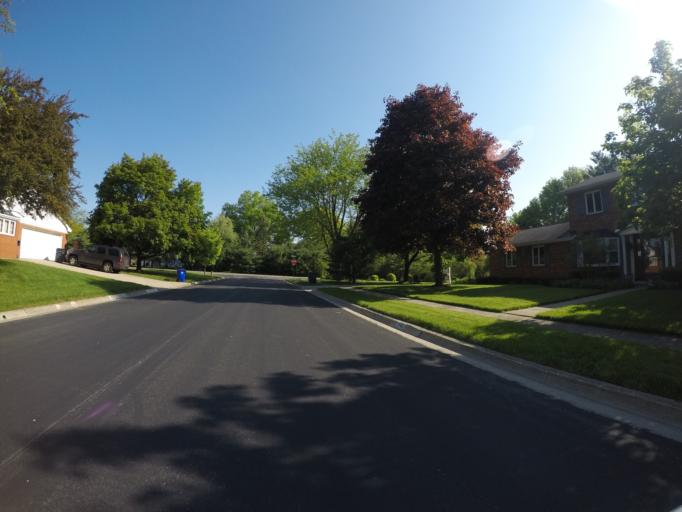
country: US
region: Ohio
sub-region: Franklin County
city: Upper Arlington
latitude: 40.0395
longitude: -83.0467
